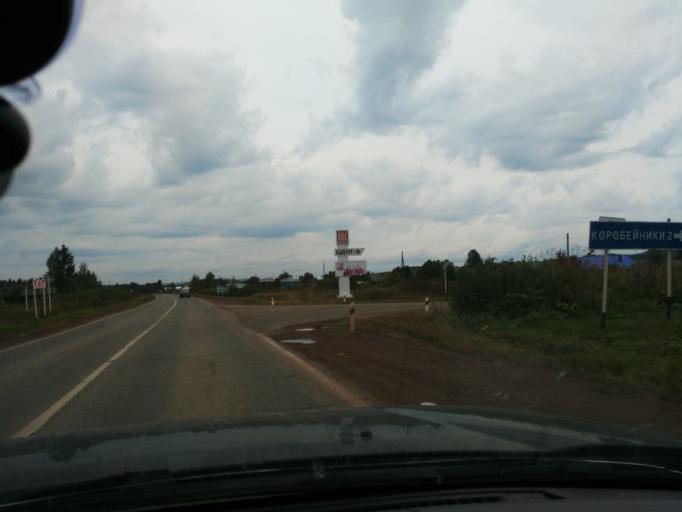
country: RU
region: Perm
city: Chernushka
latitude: 56.7285
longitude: 56.1779
